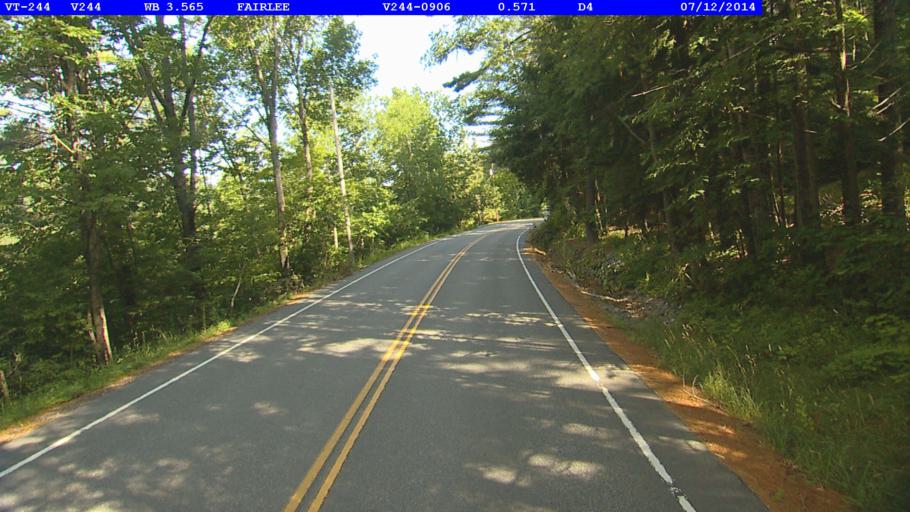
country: US
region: New Hampshire
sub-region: Grafton County
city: Orford
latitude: 43.8966
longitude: -72.2084
